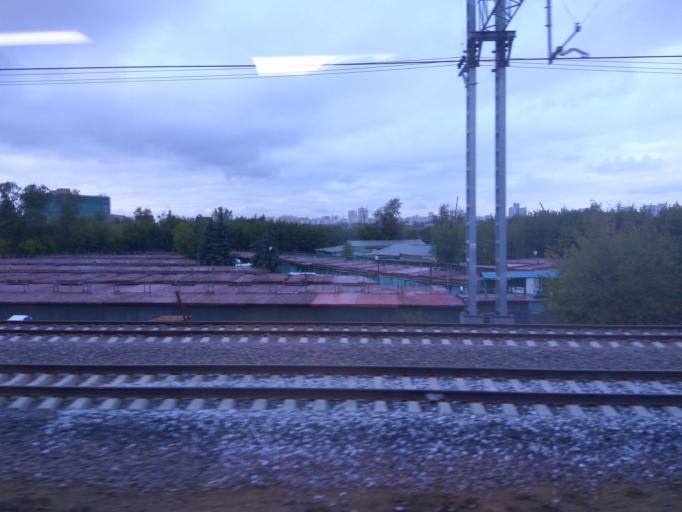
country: RU
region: Moscow
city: Likhobory
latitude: 55.8467
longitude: 37.5499
